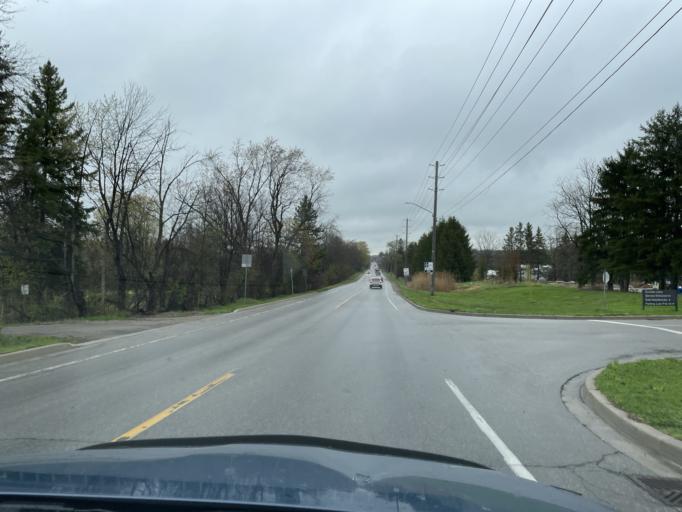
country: CA
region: Ontario
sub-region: Wellington County
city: Guelph
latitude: 43.5378
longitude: -80.2248
